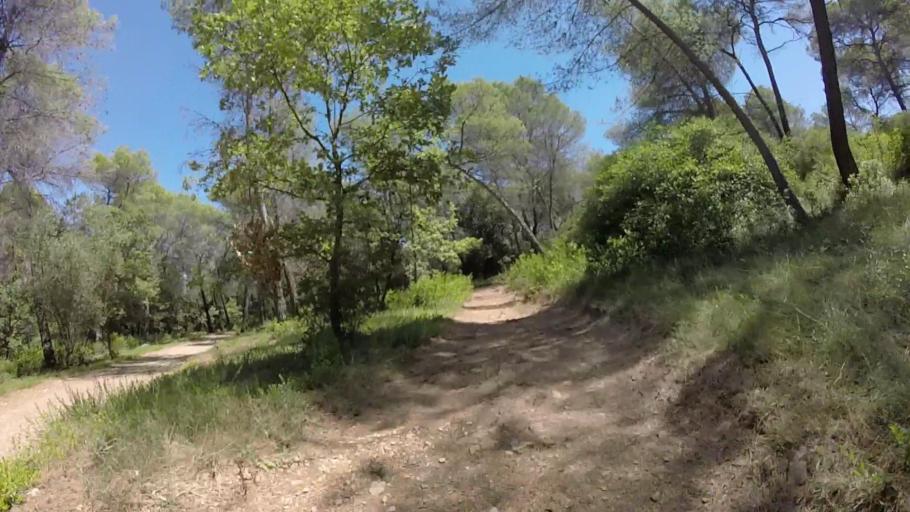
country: FR
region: Provence-Alpes-Cote d'Azur
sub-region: Departement des Alpes-Maritimes
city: Vallauris
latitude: 43.6091
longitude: 7.0399
